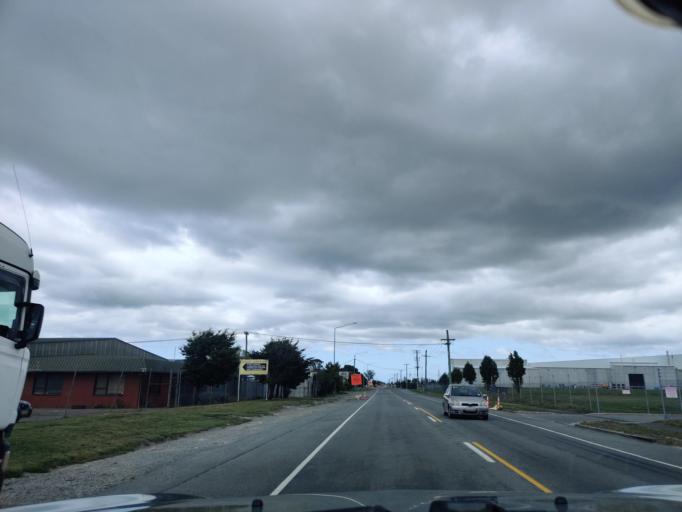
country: NZ
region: Canterbury
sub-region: Selwyn District
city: Prebbleton
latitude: -43.5526
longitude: 172.5151
